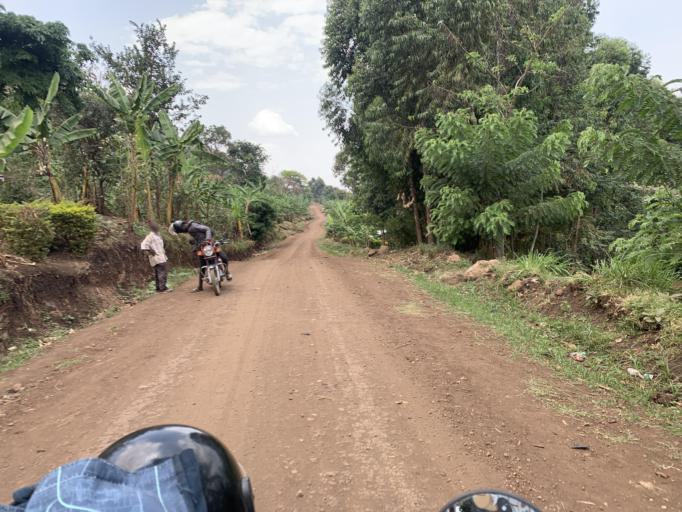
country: UG
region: Eastern Region
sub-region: Sironko District
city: Sironko
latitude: 1.2568
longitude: 34.3110
